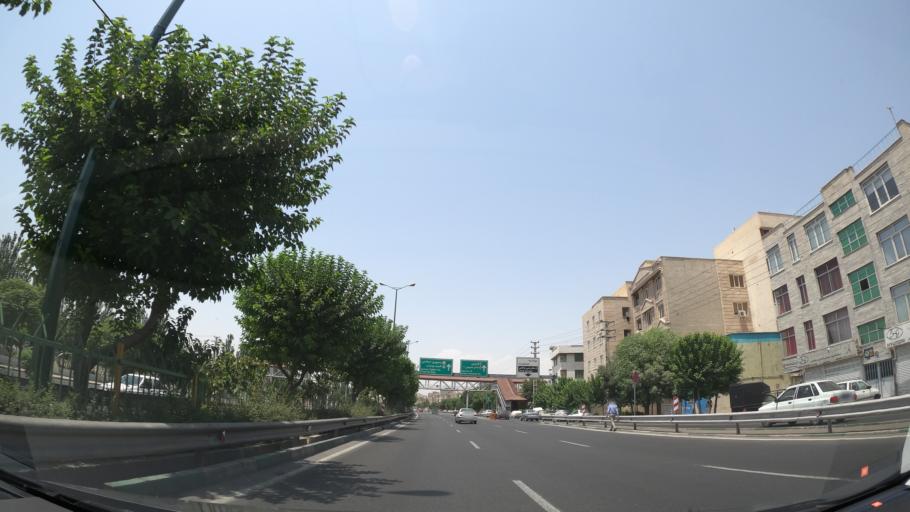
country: IR
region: Tehran
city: Tehran
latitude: 35.6485
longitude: 51.3904
